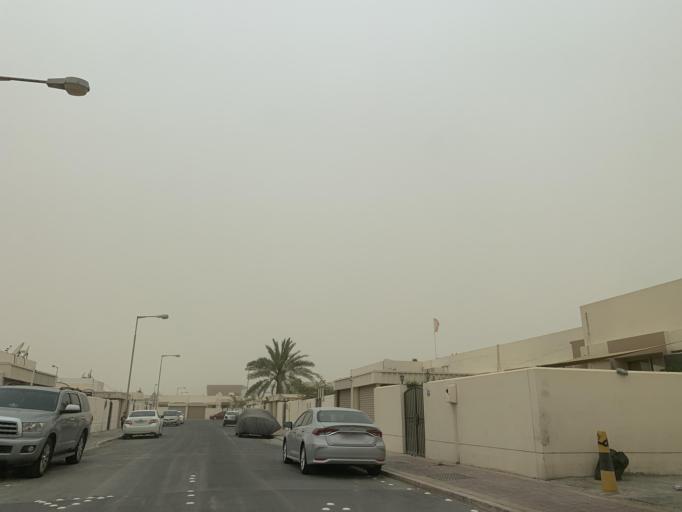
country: BH
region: Central Governorate
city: Madinat Hamad
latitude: 26.1327
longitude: 50.5197
